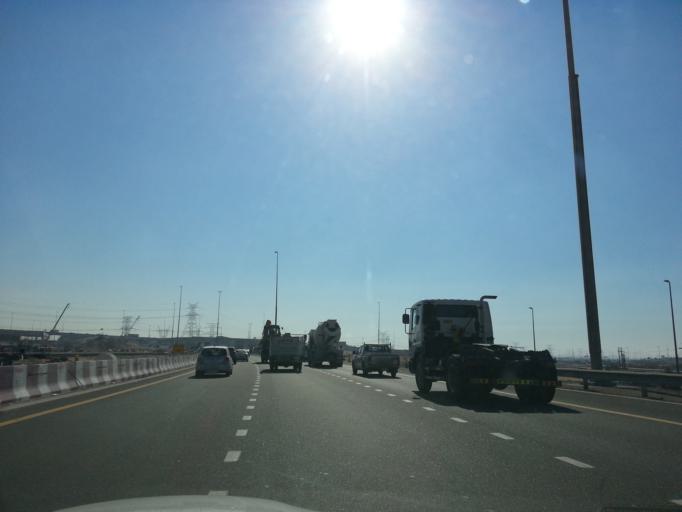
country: AE
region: Dubai
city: Dubai
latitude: 25.0216
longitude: 55.1604
